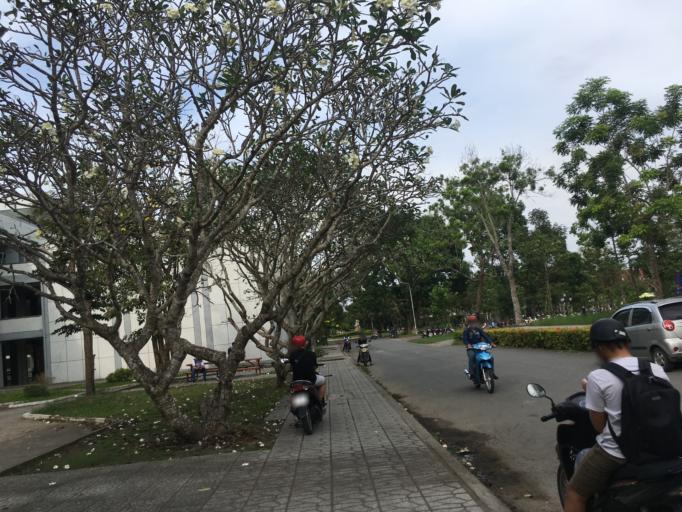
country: VN
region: Can Tho
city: Can Tho
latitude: 10.0304
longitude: 105.7701
